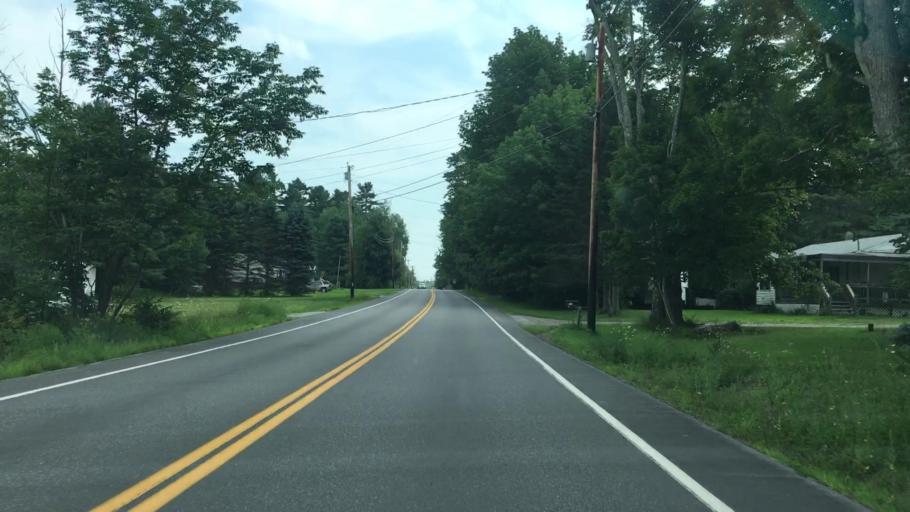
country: US
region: Maine
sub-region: Kennebec County
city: Windsor
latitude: 44.3154
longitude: -69.5821
